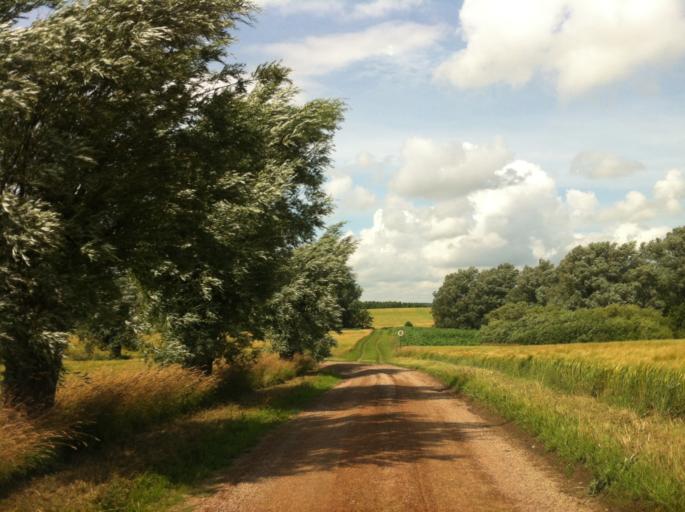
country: SE
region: Skane
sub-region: Skurups Kommun
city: Skurup
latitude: 55.4451
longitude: 13.4382
